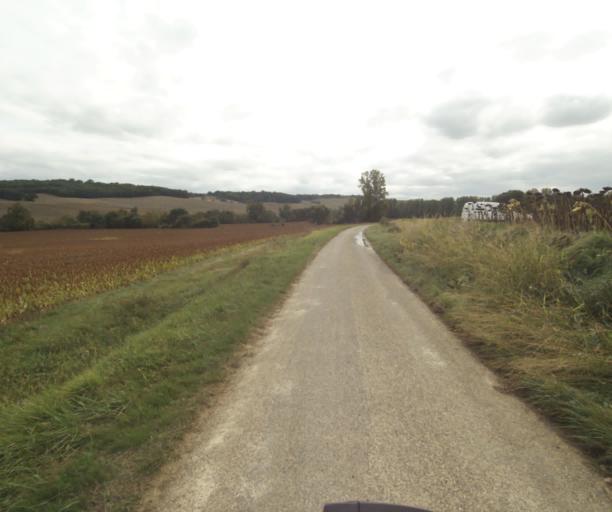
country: FR
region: Midi-Pyrenees
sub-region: Departement du Tarn-et-Garonne
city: Beaumont-de-Lomagne
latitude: 43.8201
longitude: 1.0836
